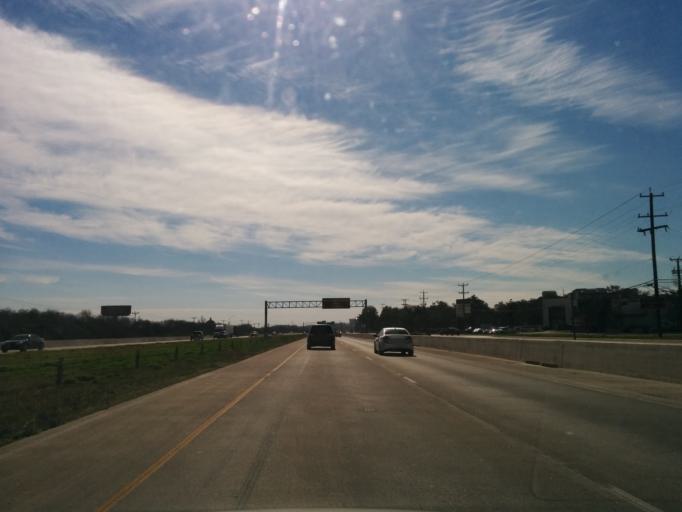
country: US
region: Texas
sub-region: Bexar County
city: Cross Mountain
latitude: 29.6407
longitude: -98.6176
